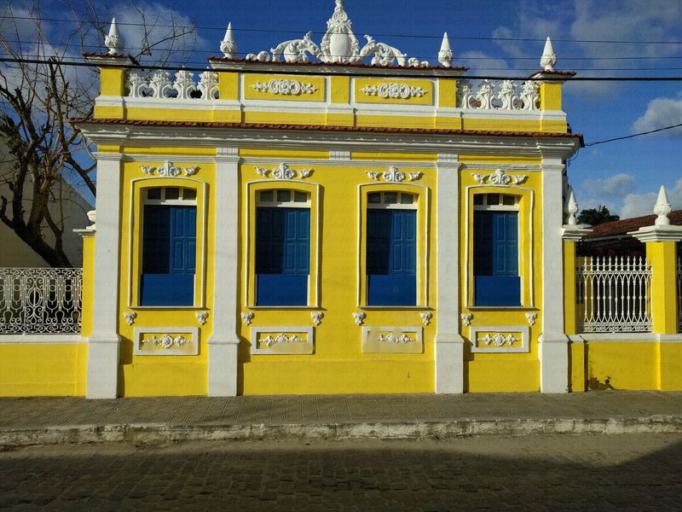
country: BR
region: Bahia
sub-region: Nova Vicosa
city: Nova Vicosa
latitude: -17.7379
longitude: -39.2591
